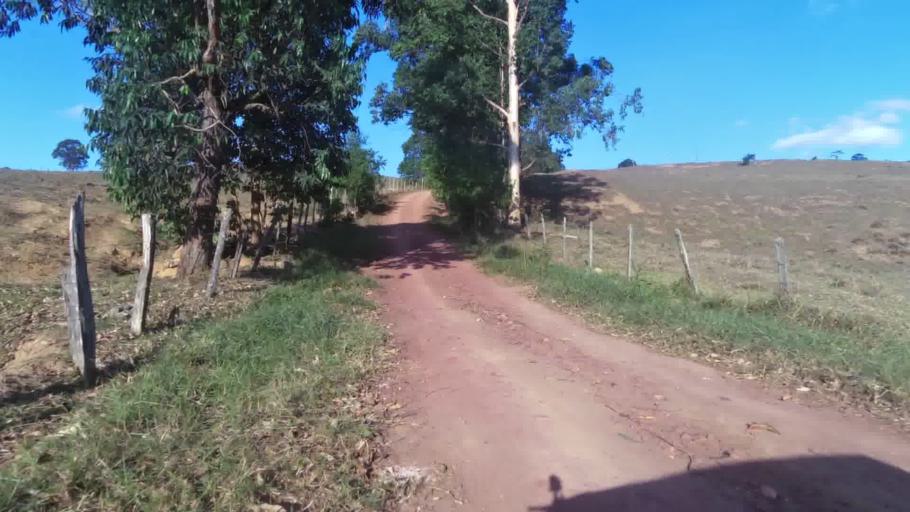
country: BR
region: Espirito Santo
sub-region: Marataizes
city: Marataizes
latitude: -21.1662
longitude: -41.0514
